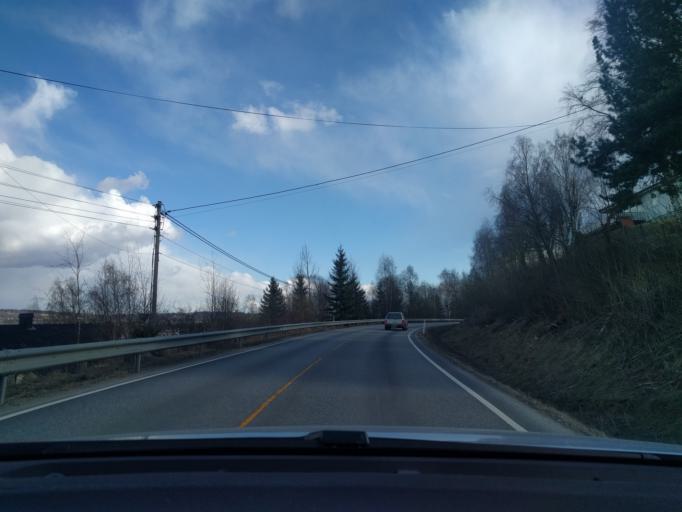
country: NO
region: Hedmark
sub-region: Ringsaker
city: Brumunddal
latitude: 60.8697
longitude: 10.9071
